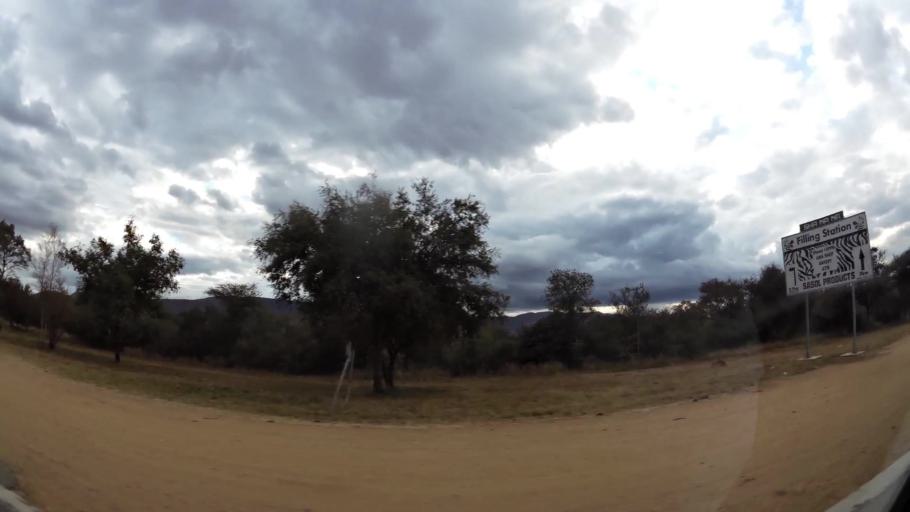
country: ZA
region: Limpopo
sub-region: Waterberg District Municipality
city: Mokopane
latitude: -24.2138
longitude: 29.0057
